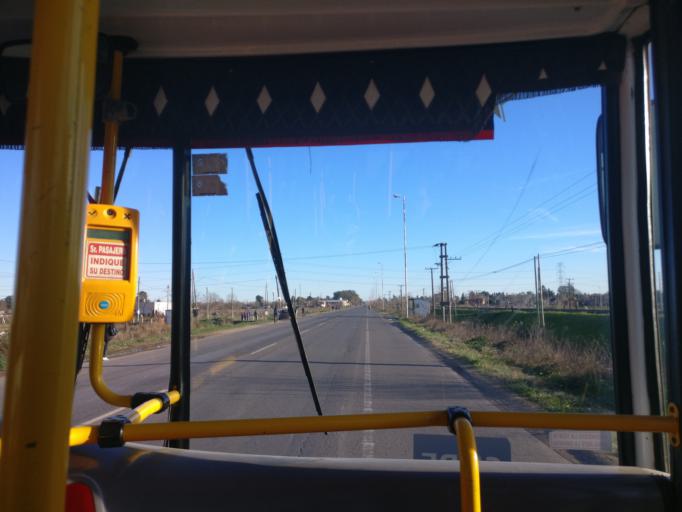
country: AR
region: Buenos Aires
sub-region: Partido de Ezeiza
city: Ezeiza
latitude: -34.9269
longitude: -58.6120
